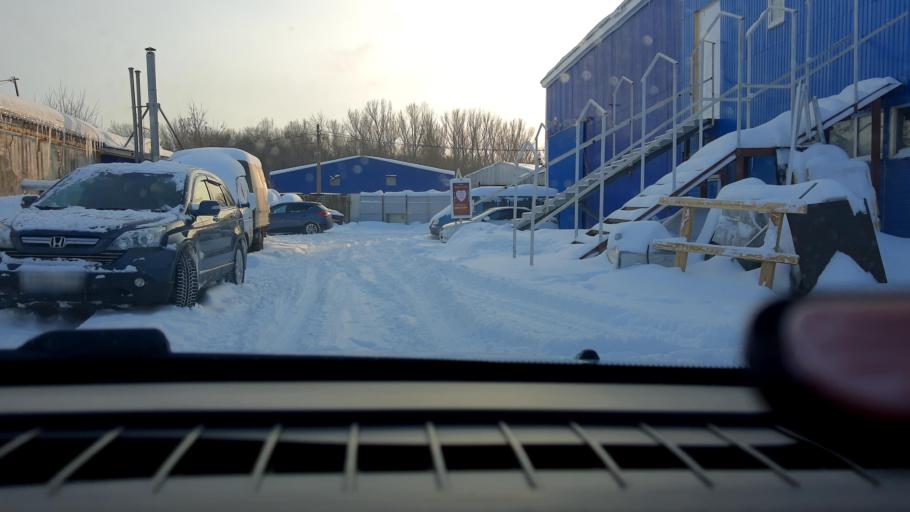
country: RU
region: Nizjnij Novgorod
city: Gorbatovka
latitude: 56.2230
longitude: 43.8097
